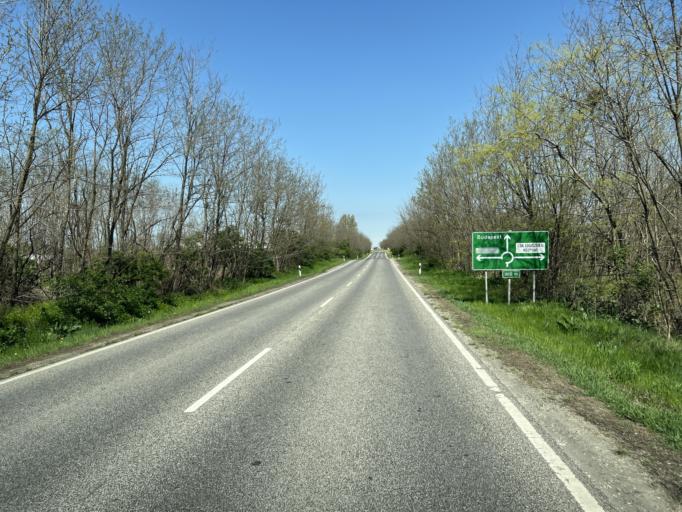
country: HU
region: Pest
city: Alsonemedi
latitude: 47.3378
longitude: 19.1772
